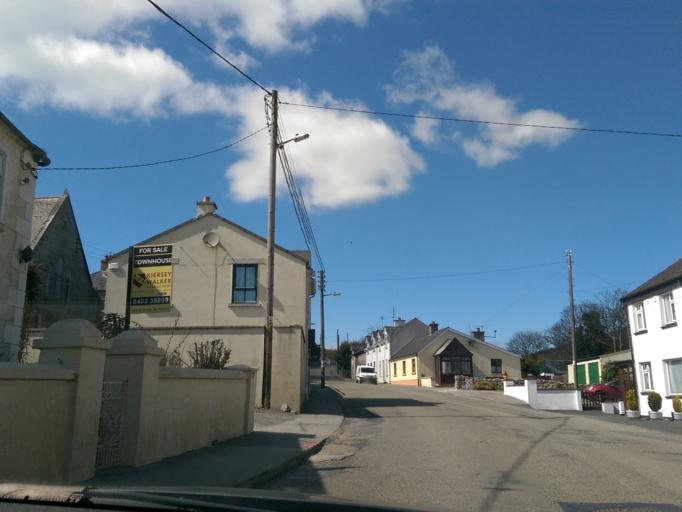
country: IE
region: Leinster
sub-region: Wicklow
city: Carnew
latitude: 52.8006
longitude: -6.4658
